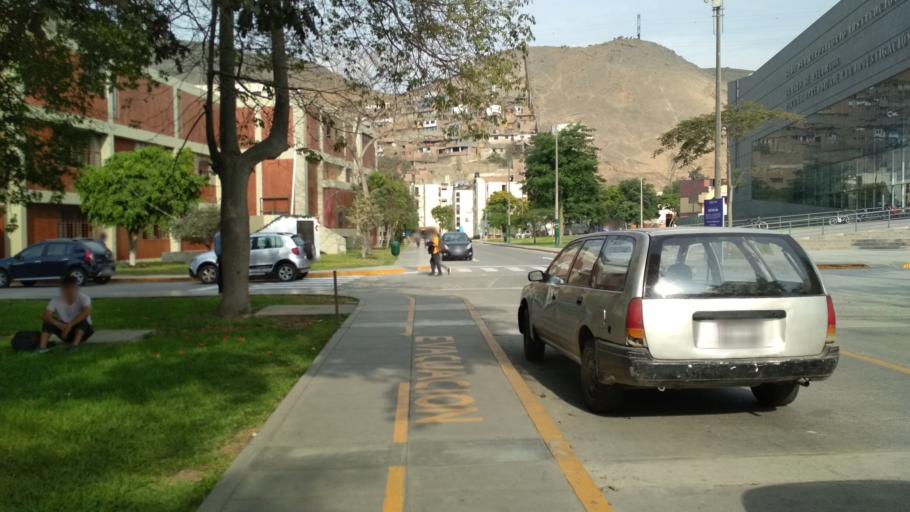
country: PE
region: Lima
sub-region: Lima
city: Independencia
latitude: -12.0178
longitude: -77.0499
